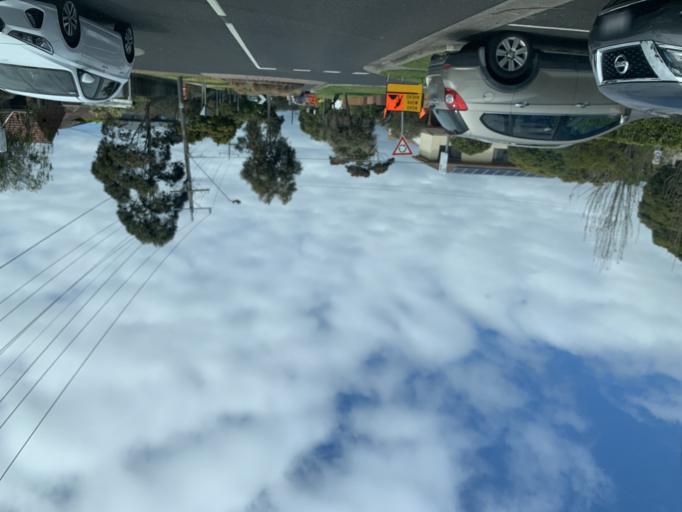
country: AU
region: Victoria
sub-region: Kingston
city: Mentone
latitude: -37.9836
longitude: 145.0685
